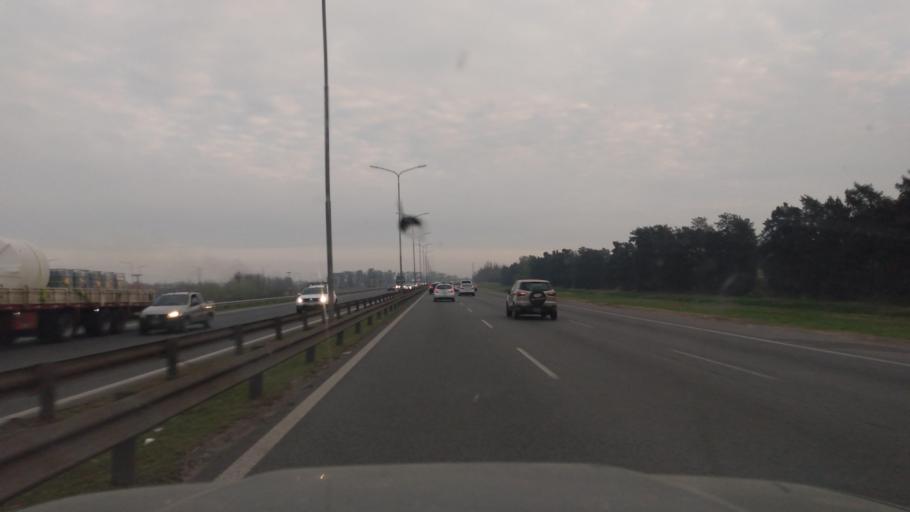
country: AR
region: Buenos Aires
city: Hurlingham
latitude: -34.5404
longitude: -58.6004
